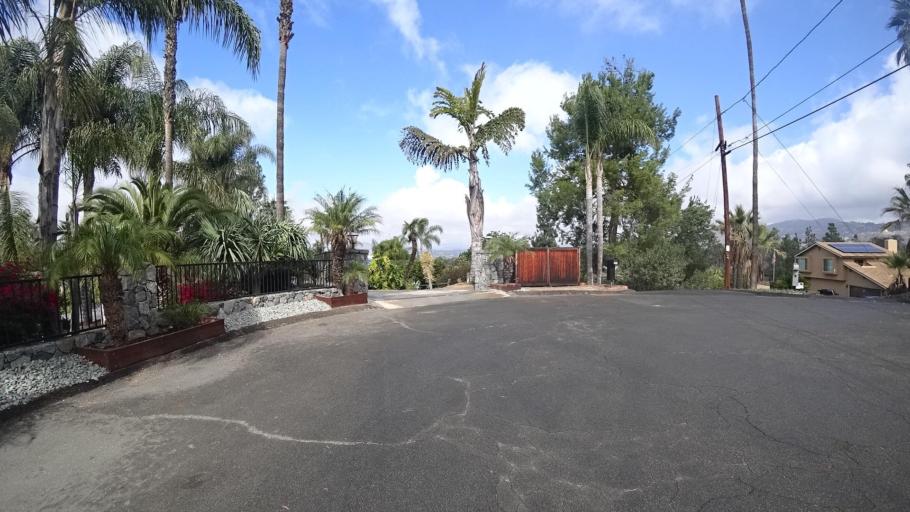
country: US
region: California
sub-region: San Diego County
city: Granite Hills
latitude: 32.7832
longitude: -116.9099
